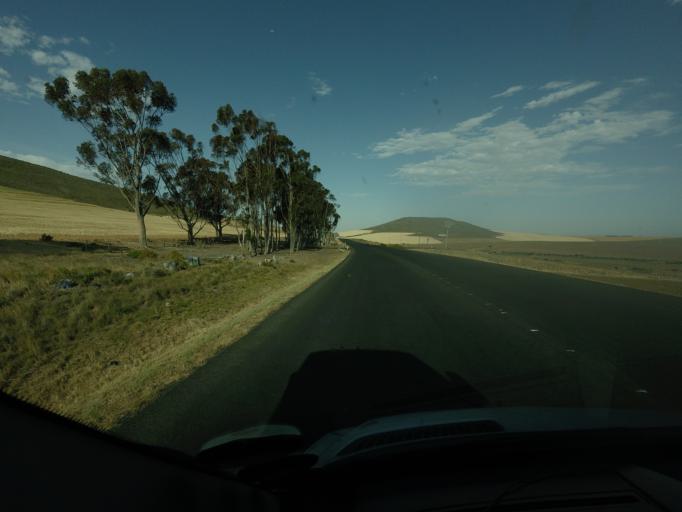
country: ZA
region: Western Cape
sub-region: Overberg District Municipality
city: Swellendam
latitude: -34.1055
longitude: 20.2372
